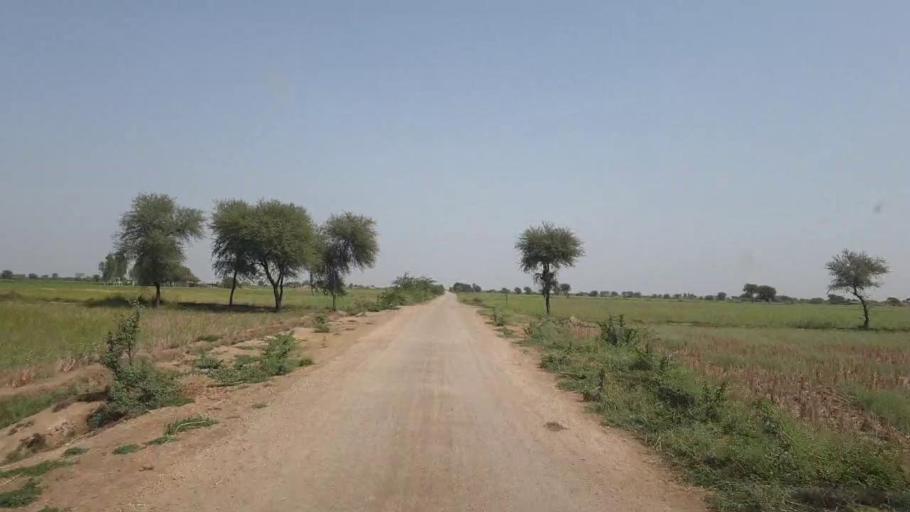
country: PK
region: Sindh
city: Jati
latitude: 24.4774
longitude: 68.5656
